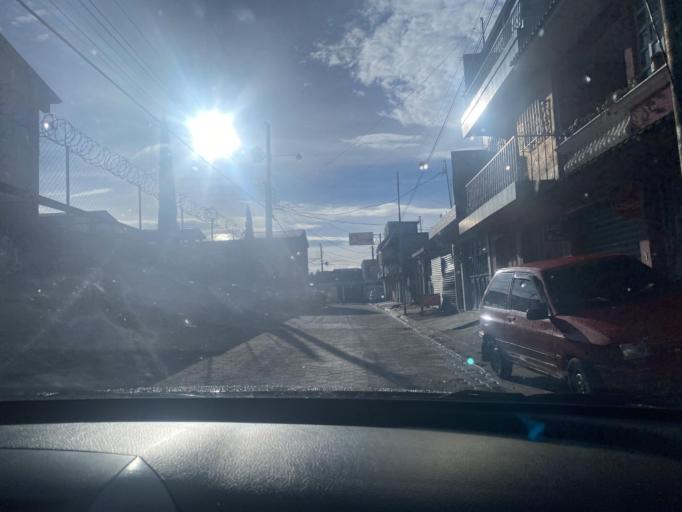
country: GT
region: Quetzaltenango
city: Olintepeque
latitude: 14.8657
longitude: -91.5193
